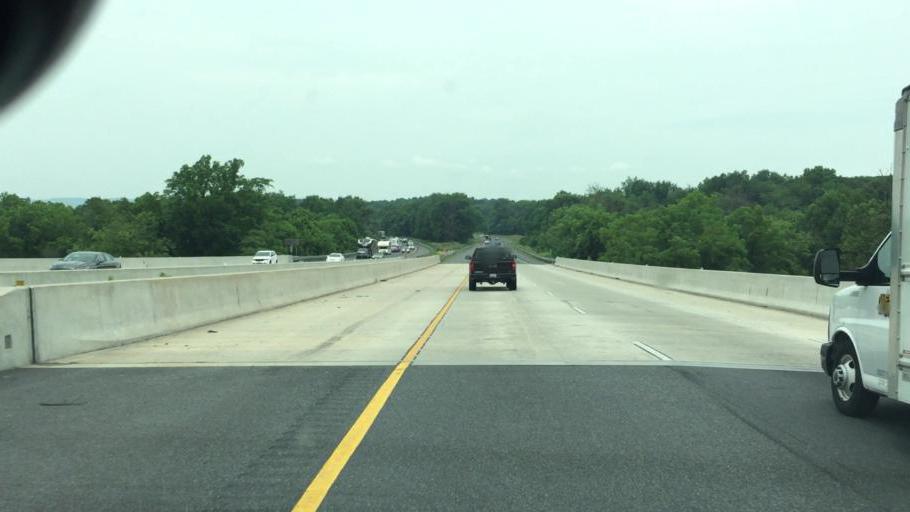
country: US
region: Maryland
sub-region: Washington County
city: Wilson-Conococheague
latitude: 39.6414
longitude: -77.8287
